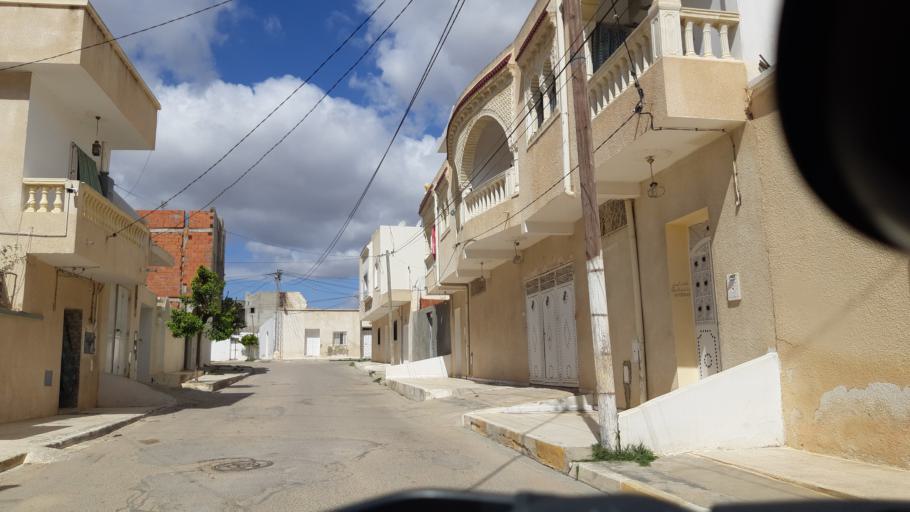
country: TN
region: Susah
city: Akouda
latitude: 35.8783
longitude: 10.5349
